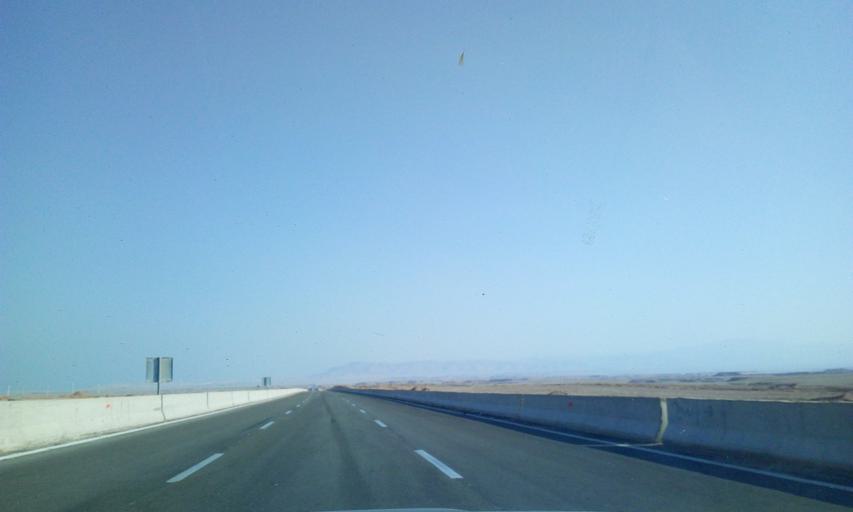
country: EG
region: As Suways
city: Ain Sukhna
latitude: 29.1952
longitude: 32.4966
